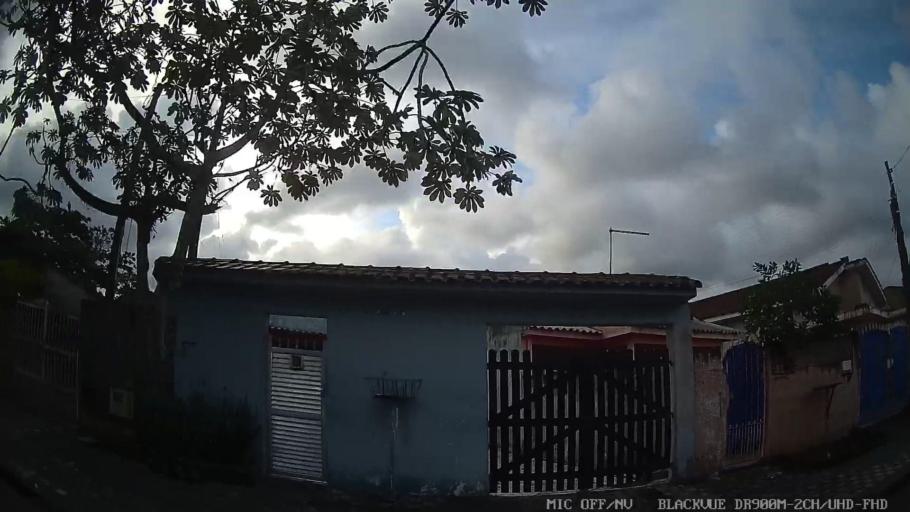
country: BR
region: Sao Paulo
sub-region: Mongagua
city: Mongagua
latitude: -24.1189
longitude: -46.6755
